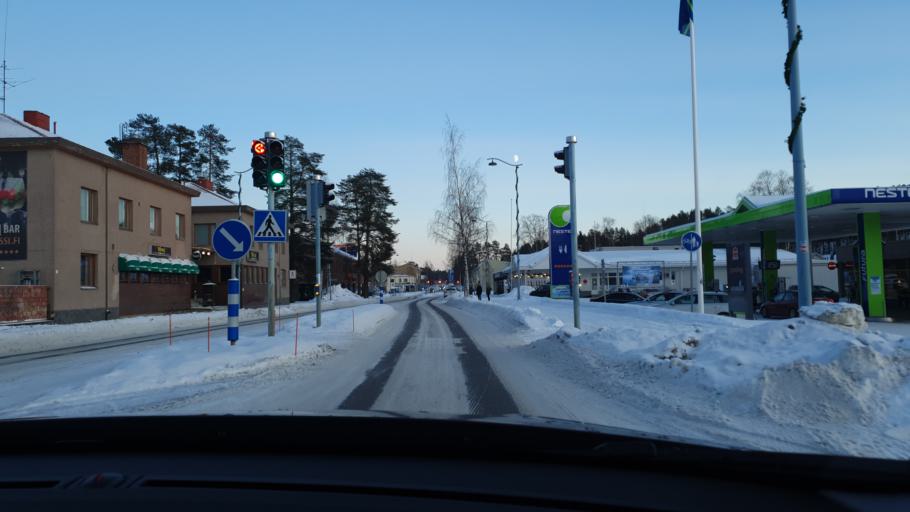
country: FI
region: Kainuu
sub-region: Kajaani
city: Sotkamo
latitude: 64.1303
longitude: 28.3798
